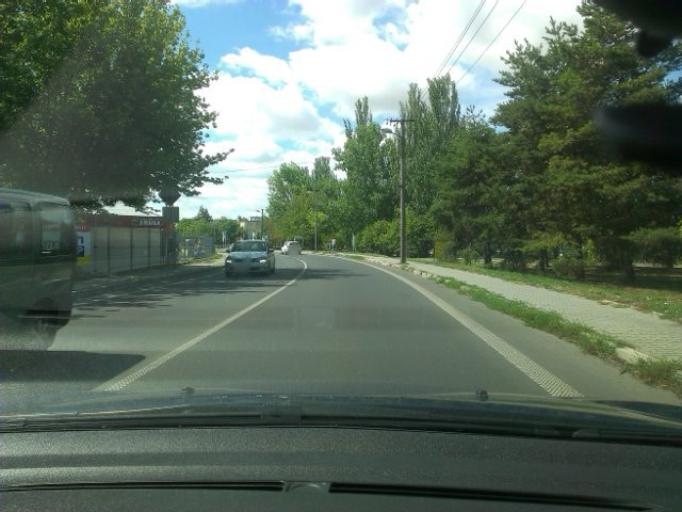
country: SK
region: Trnavsky
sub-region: Okres Trnava
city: Piestany
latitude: 48.5992
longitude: 17.8263
